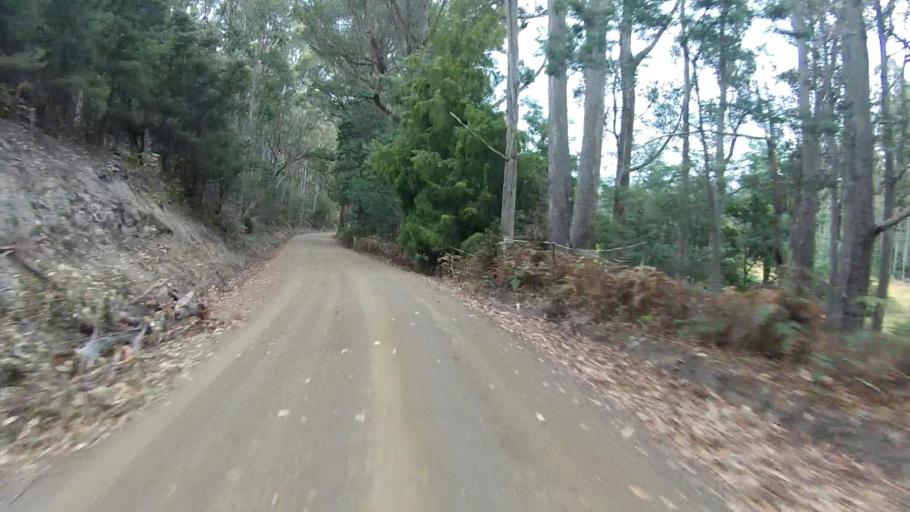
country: AU
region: Tasmania
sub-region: Huon Valley
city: Cygnet
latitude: -43.2296
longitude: 147.1605
